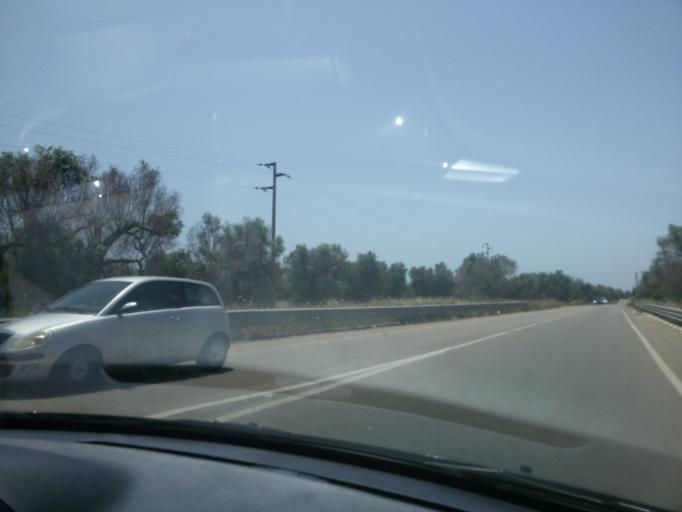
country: IT
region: Apulia
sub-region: Provincia di Lecce
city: Veglie
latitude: 40.3264
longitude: 17.9247
